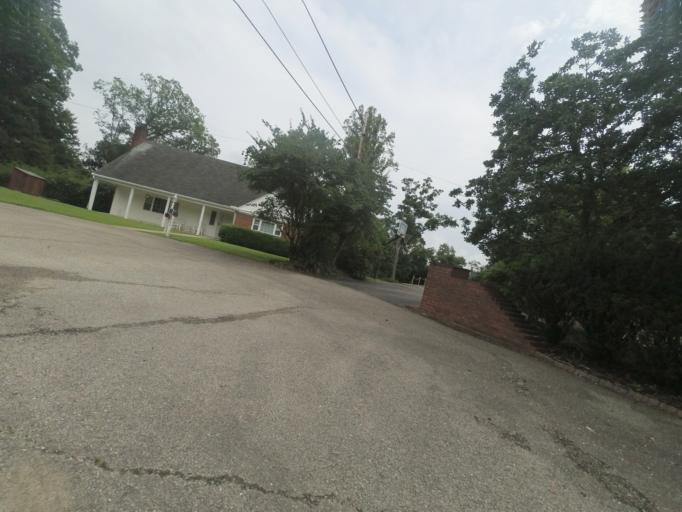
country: US
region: West Virginia
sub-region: Cabell County
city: Huntington
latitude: 38.3956
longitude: -82.4425
